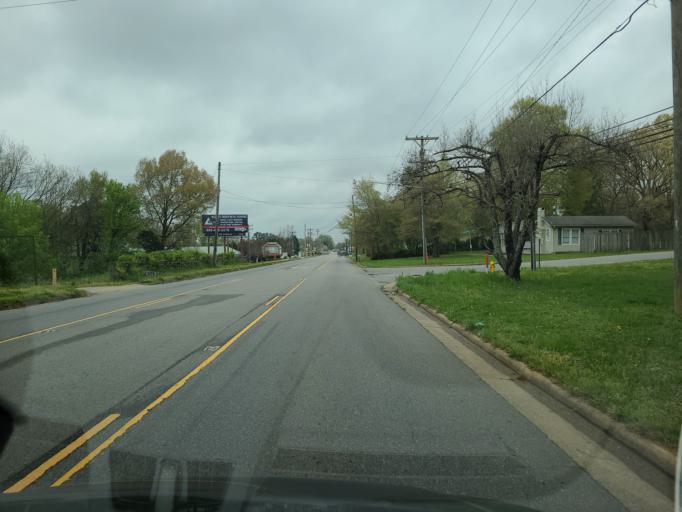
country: US
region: North Carolina
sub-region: Lincoln County
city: Lincolnton
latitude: 35.4977
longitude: -81.2432
